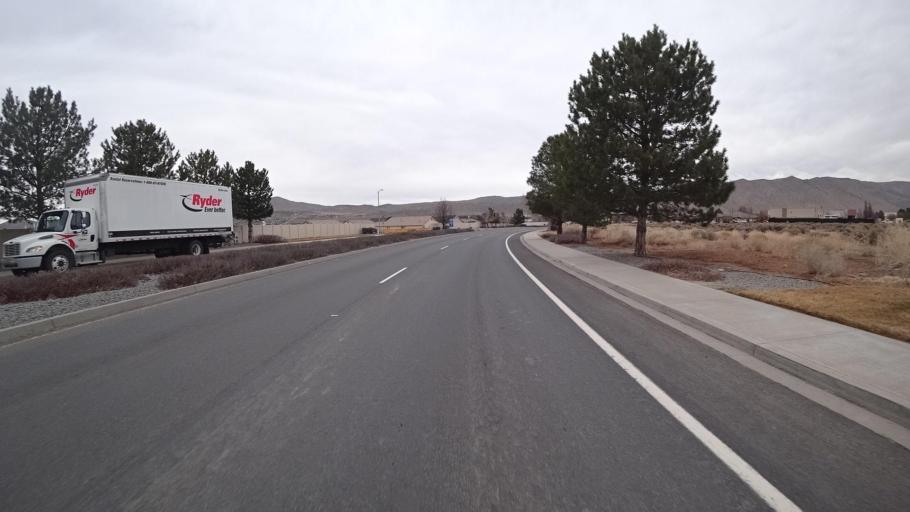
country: US
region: Nevada
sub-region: Washoe County
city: Spanish Springs
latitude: 39.6666
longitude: -119.7048
